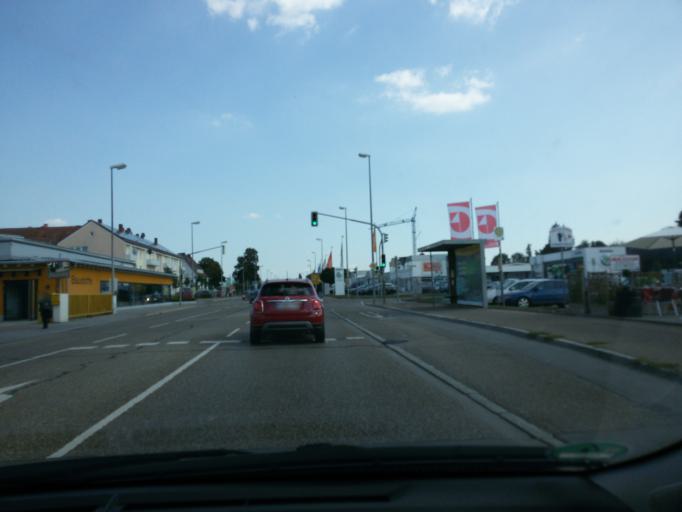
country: DE
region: Bavaria
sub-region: Swabia
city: Noerdlingen
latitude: 48.8449
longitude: 10.5012
